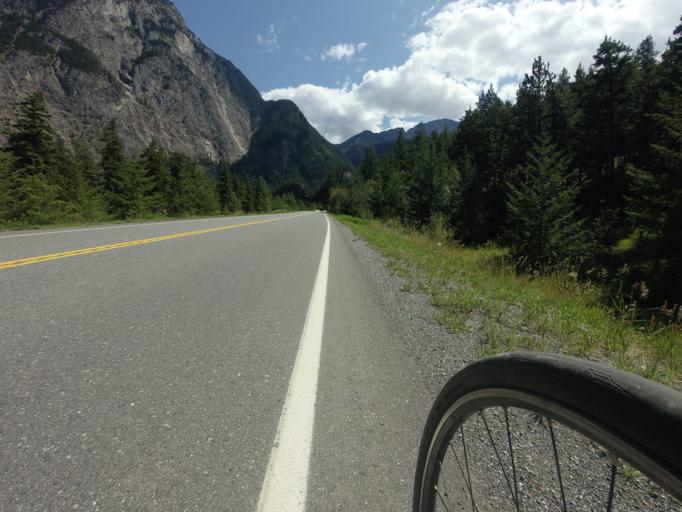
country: CA
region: British Columbia
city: Lillooet
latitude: 50.6636
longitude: -121.9880
